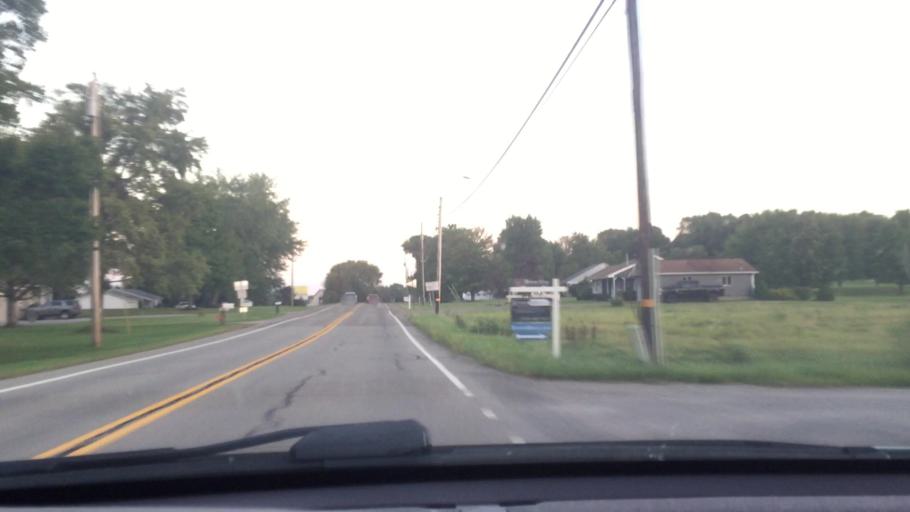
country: US
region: Pennsylvania
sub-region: Butler County
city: Slippery Rock
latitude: 41.1139
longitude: -80.0567
